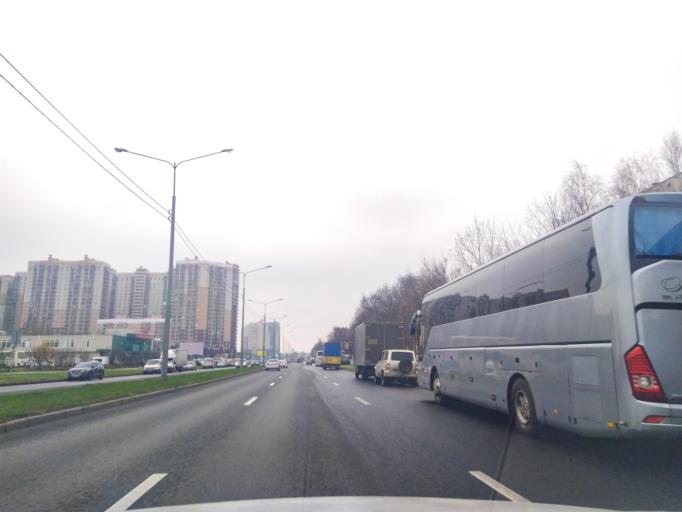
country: RU
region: St.-Petersburg
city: Sosnovka
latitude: 60.0311
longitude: 30.3393
